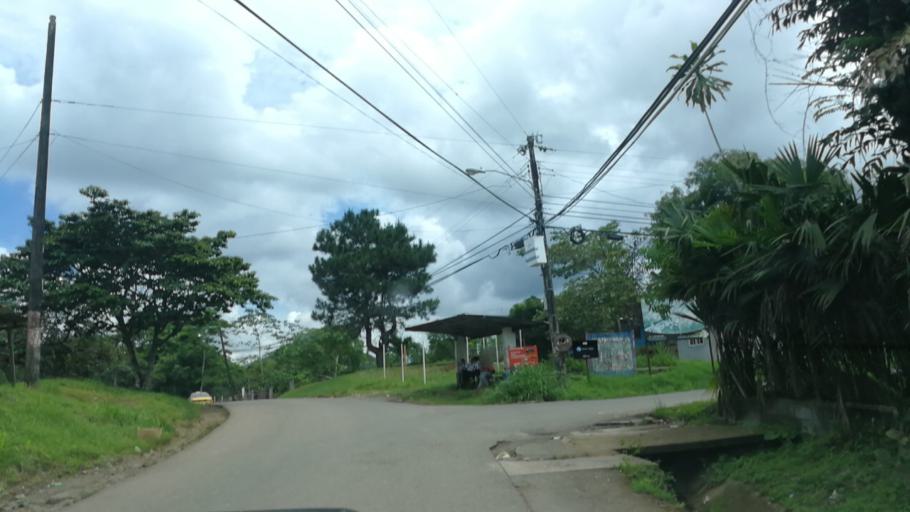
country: PA
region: Panama
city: San Miguelito
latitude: 9.0974
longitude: -79.4562
